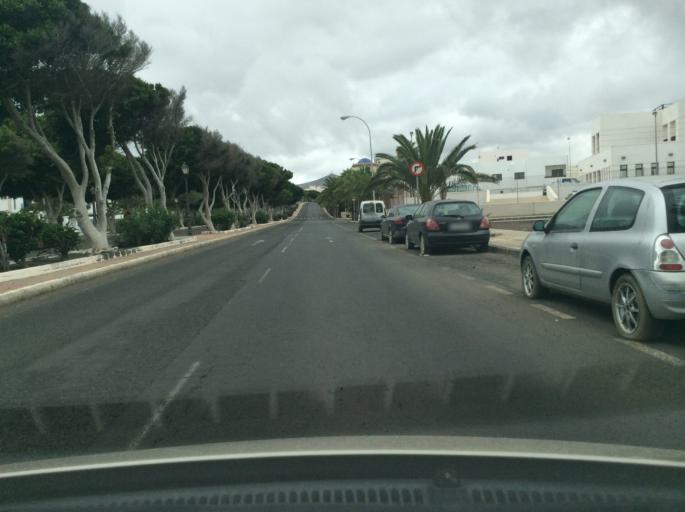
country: ES
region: Canary Islands
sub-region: Provincia de Las Palmas
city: Arrecife
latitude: 28.9656
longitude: -13.5404
